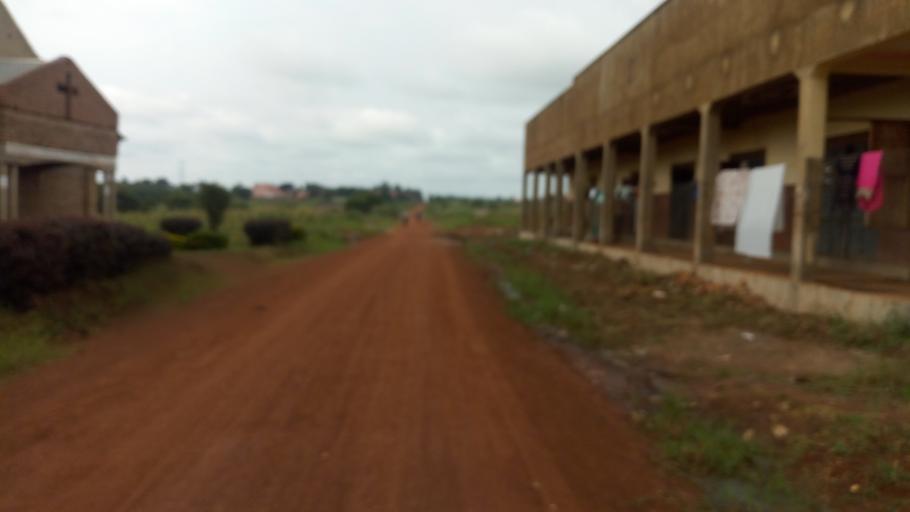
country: UG
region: Western Region
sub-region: Kiryandongo District
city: Kiryandongo
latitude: 1.8085
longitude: 32.0125
